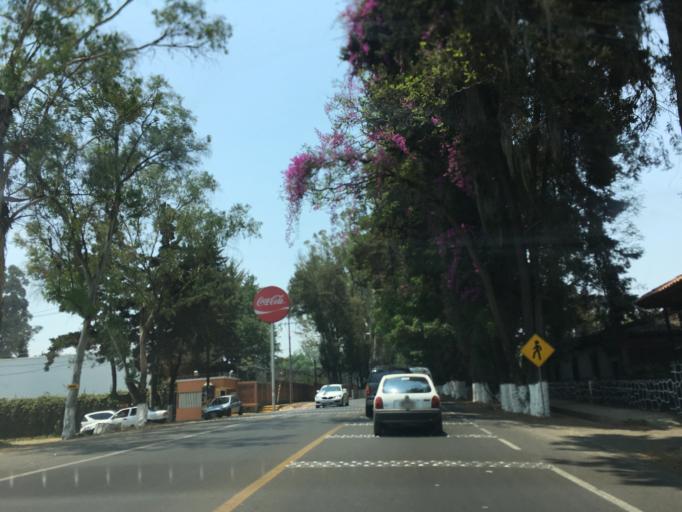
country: MX
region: Michoacan
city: Patzcuaro
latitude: 19.5361
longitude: -101.6119
